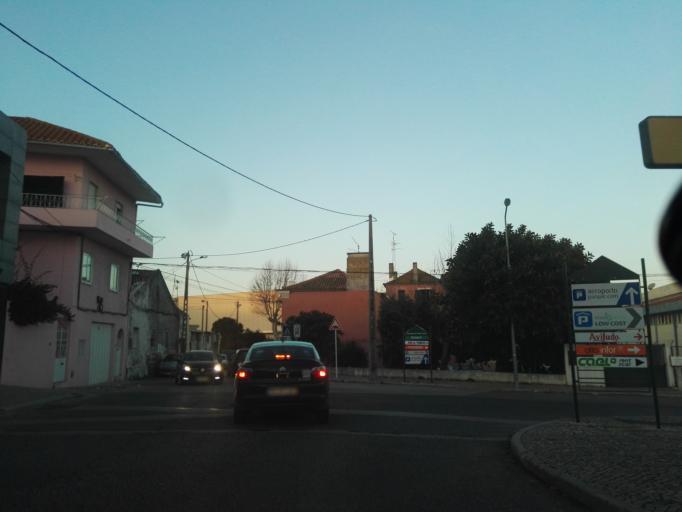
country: PT
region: Lisbon
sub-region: Loures
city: Camarate
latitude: 38.7873
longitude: -9.1290
